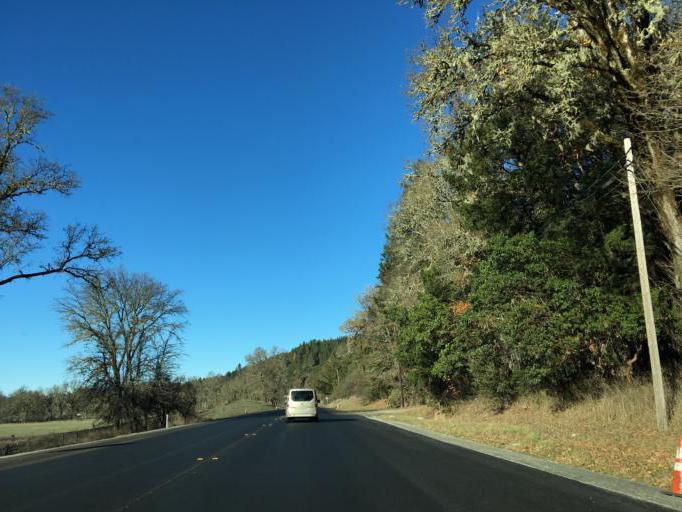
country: US
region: California
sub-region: Mendocino County
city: Laytonville
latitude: 39.6767
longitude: -123.4757
